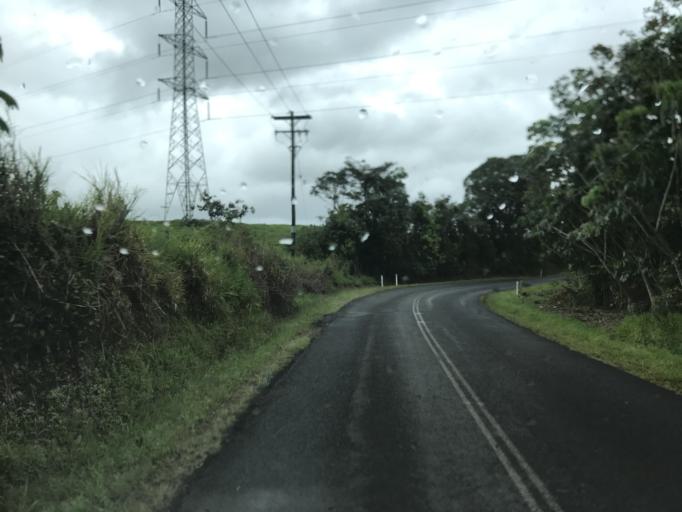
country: AU
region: Queensland
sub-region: Cassowary Coast
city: Innisfail
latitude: -17.5171
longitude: 145.9731
